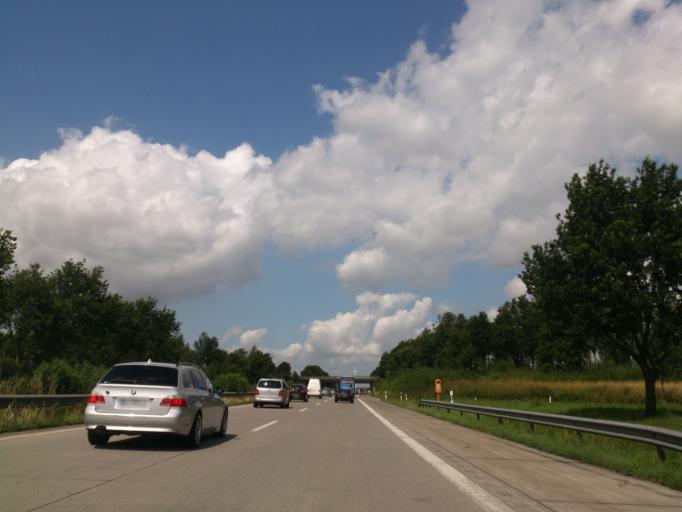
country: DE
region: Schleswig-Holstein
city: Hohenfelde
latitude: 53.8418
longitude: 9.6036
